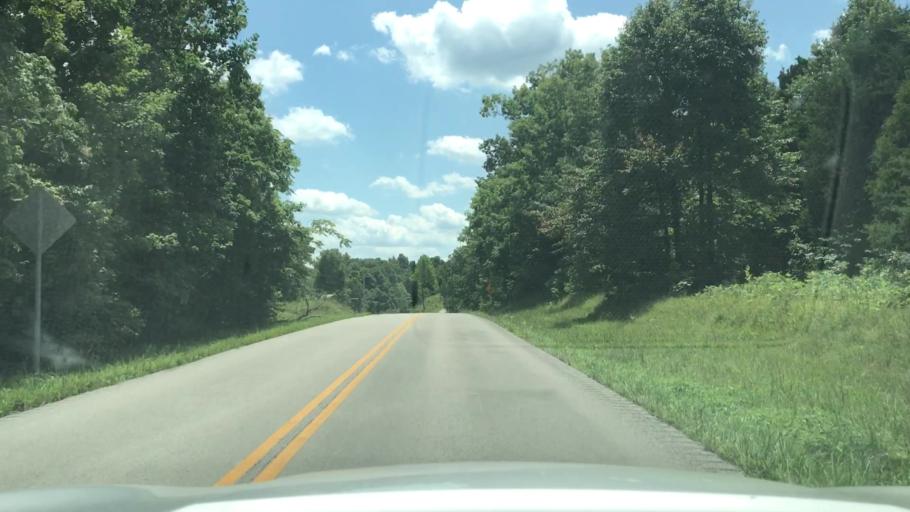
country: US
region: Kentucky
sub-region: Hopkins County
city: Nortonville
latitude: 37.1097
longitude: -87.3340
